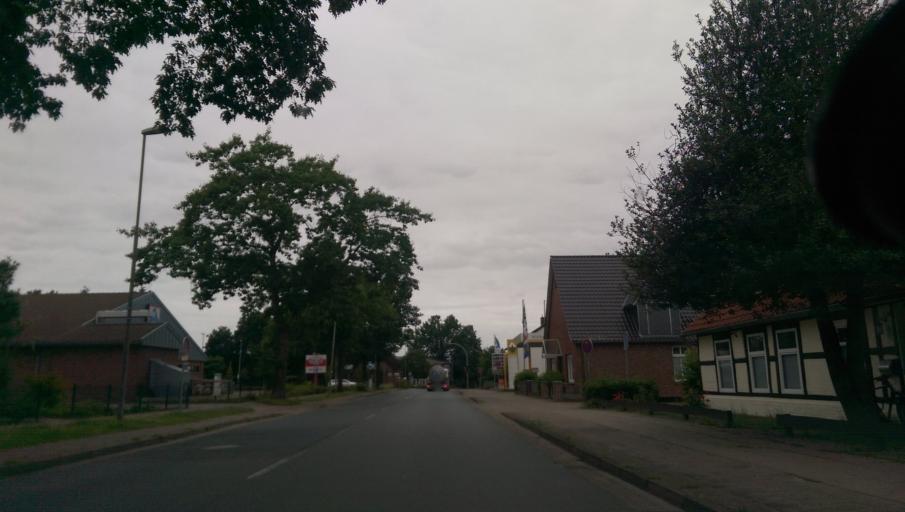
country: DE
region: Lower Saxony
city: Rotenburg
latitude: 53.1014
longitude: 9.3993
